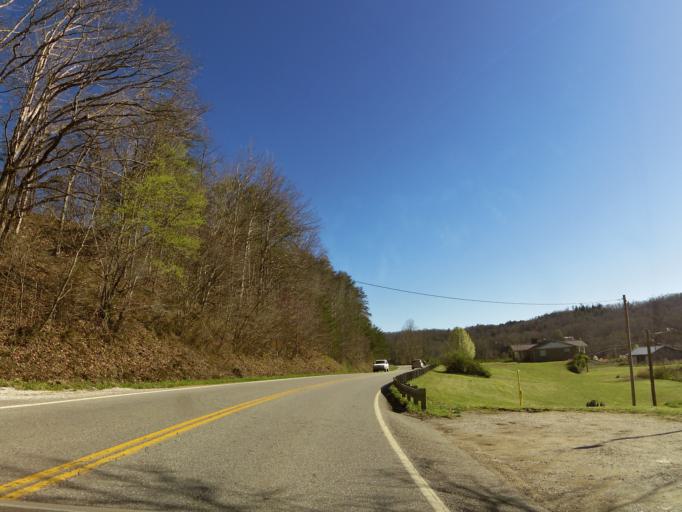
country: US
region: Tennessee
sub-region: Scott County
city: Huntsville
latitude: 36.4553
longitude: -84.4742
